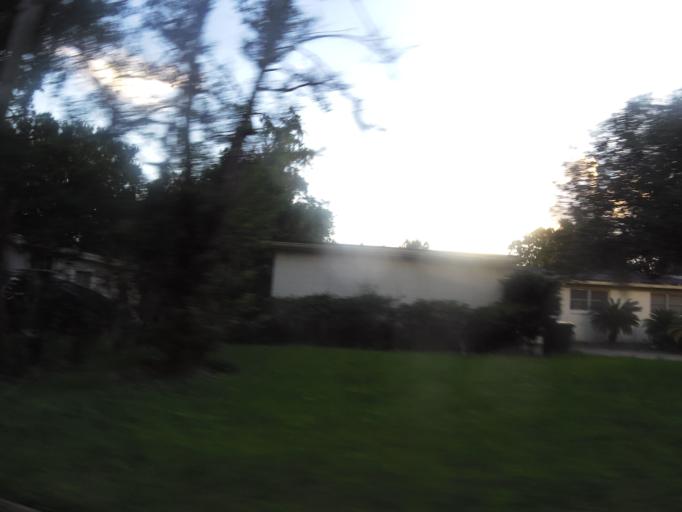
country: US
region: Florida
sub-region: Duval County
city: Jacksonville
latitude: 30.2343
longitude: -81.6125
